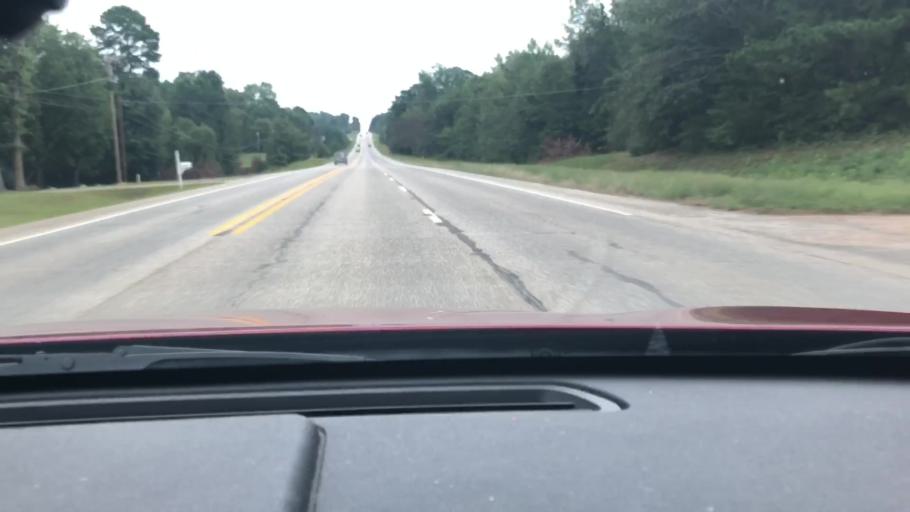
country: US
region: Arkansas
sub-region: Miller County
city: Texarkana
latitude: 33.4296
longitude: -93.9518
